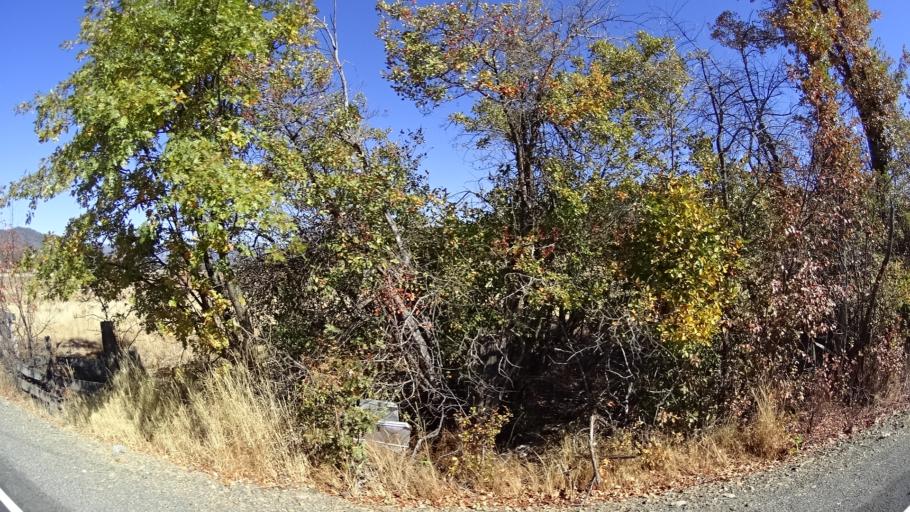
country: US
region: California
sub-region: Siskiyou County
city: Yreka
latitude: 41.5554
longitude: -122.9198
